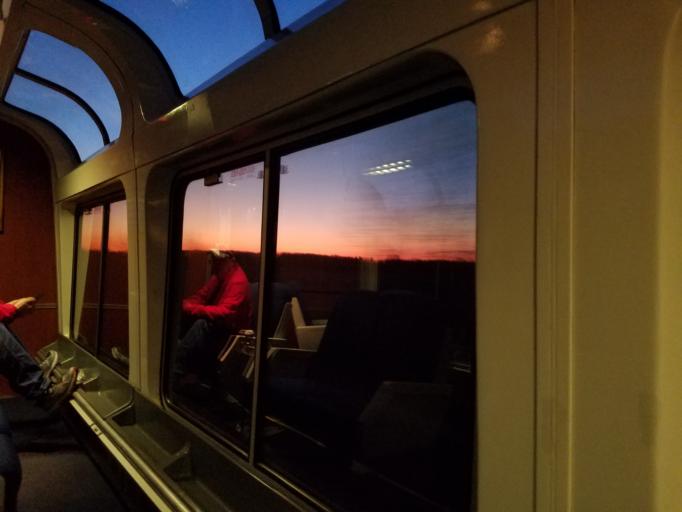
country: US
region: Ohio
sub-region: Williams County
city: Bryan
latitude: 41.4671
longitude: -84.6312
